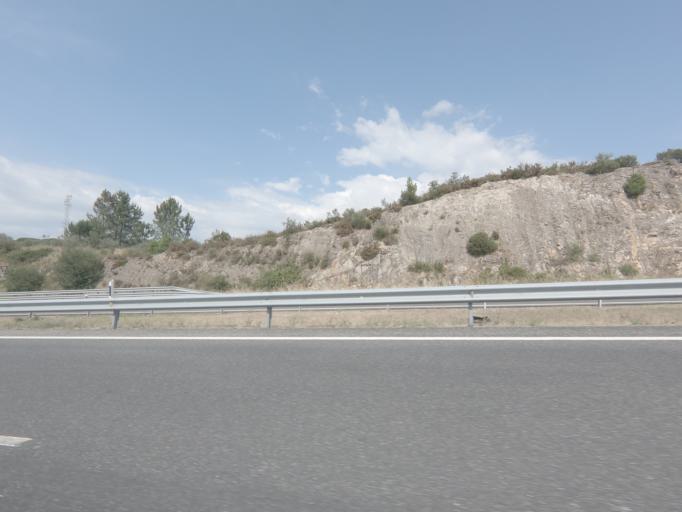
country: ES
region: Galicia
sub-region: Provincia de Ourense
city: Ourense
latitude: 42.3052
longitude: -7.8750
